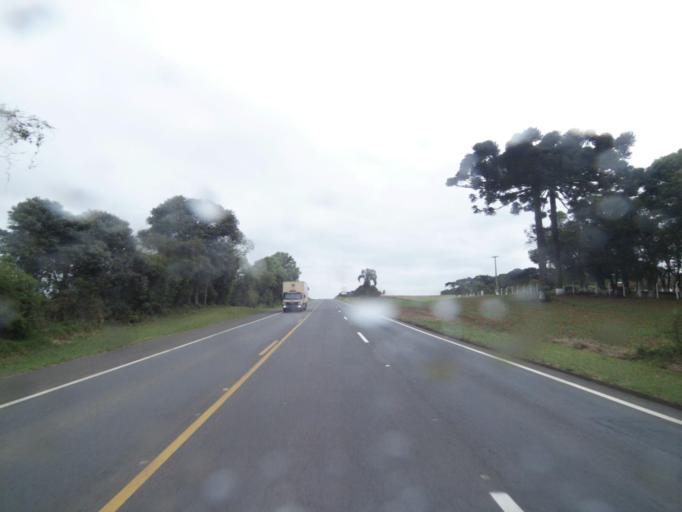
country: BR
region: Parana
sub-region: Palmeira
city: Palmeira
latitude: -25.4277
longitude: -50.1214
